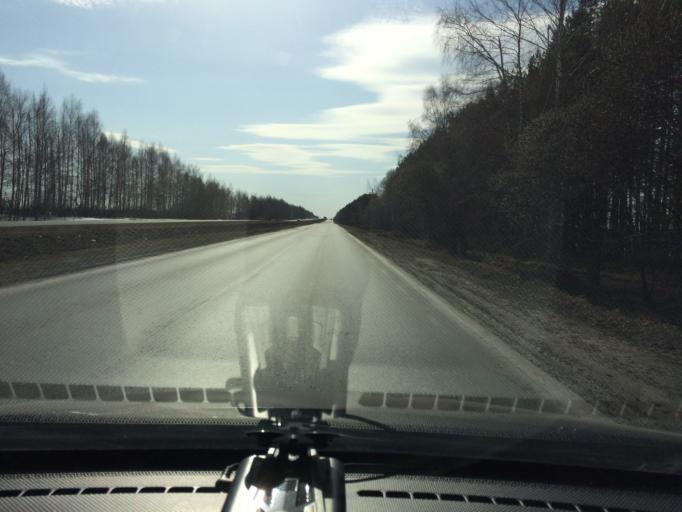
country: RU
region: Mariy-El
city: Yoshkar-Ola
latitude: 56.7302
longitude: 48.1437
